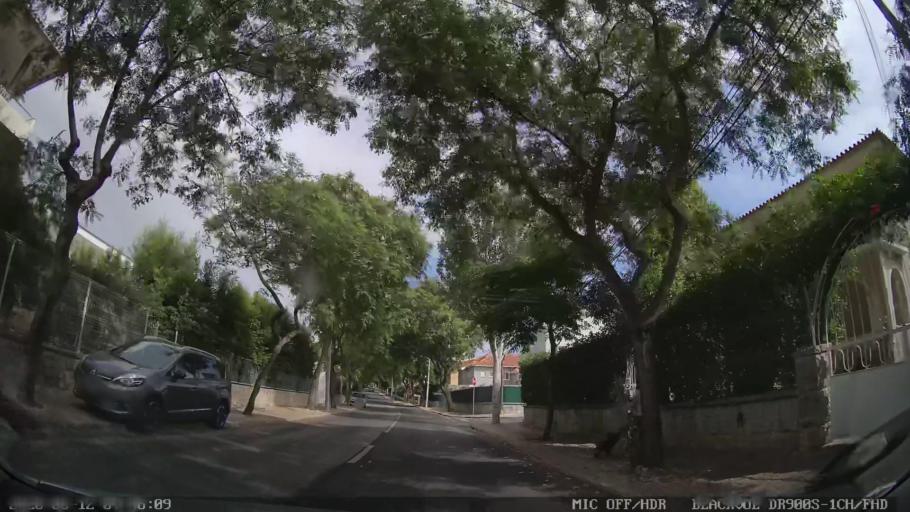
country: PT
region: Lisbon
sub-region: Cascais
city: Estoril
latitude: 38.6984
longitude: -9.3781
